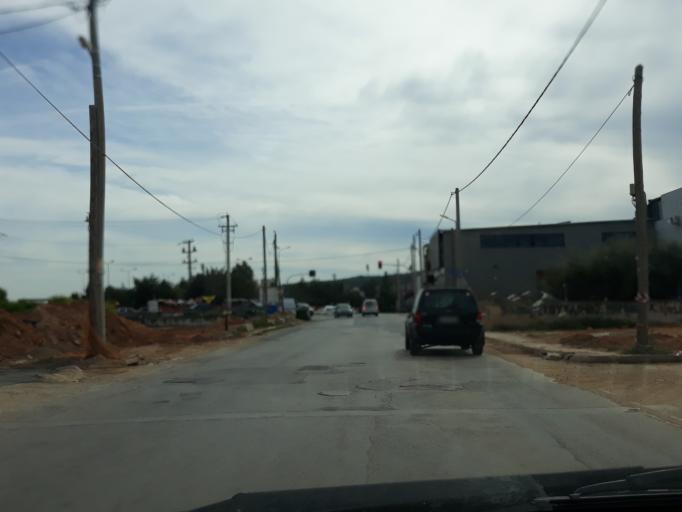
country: GR
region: Attica
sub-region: Nomarchia Dytikis Attikis
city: Ano Liosia
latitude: 38.0806
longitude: 23.7102
